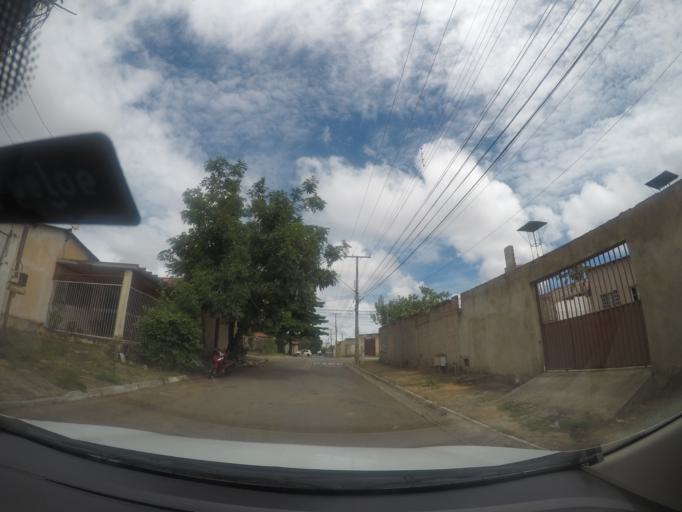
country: BR
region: Goias
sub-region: Goiania
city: Goiania
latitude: -16.6653
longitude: -49.3004
